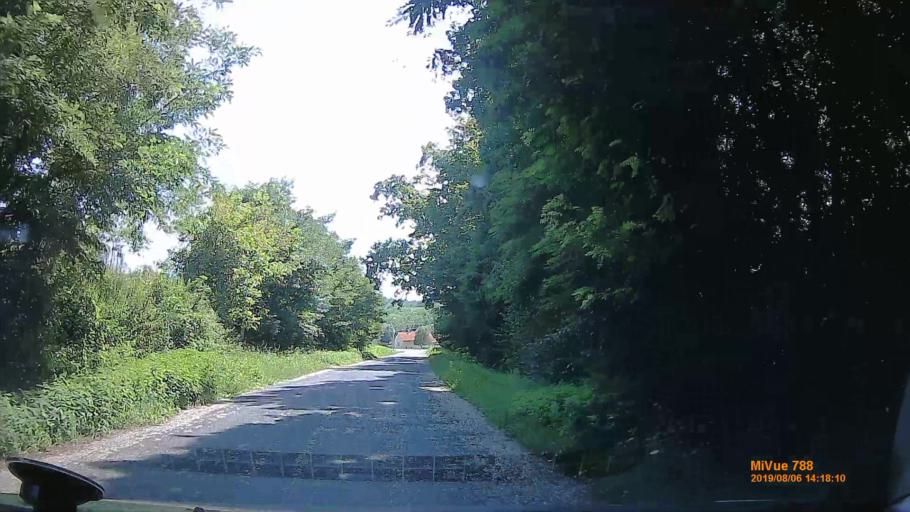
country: HU
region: Zala
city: Zalakomar
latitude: 46.5379
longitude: 17.0830
